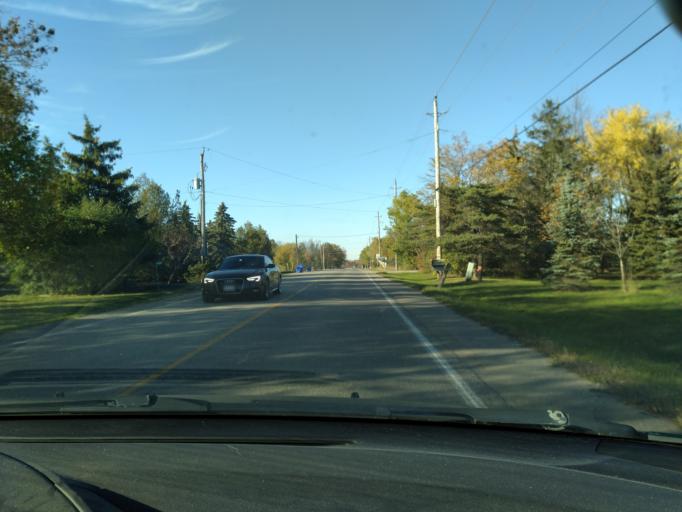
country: CA
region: Ontario
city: Vaughan
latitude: 43.8957
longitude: -79.7019
